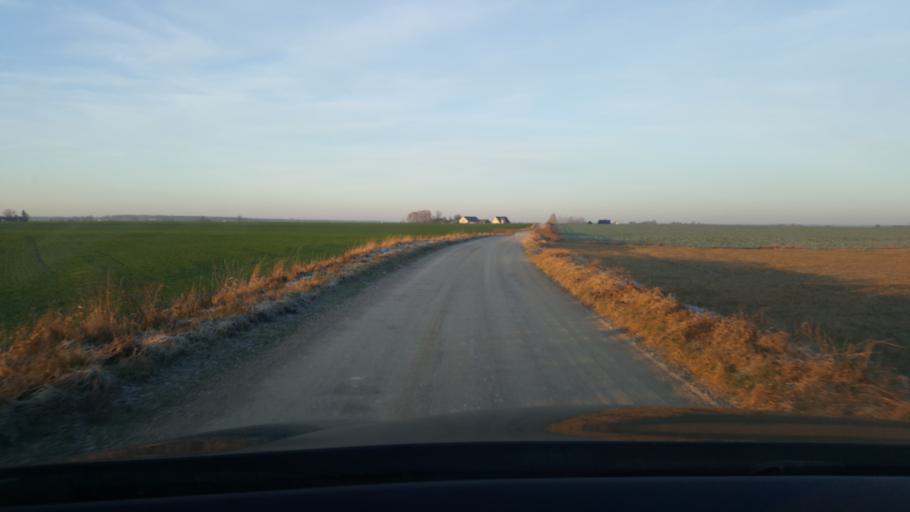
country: LT
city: Prienai
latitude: 54.4841
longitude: 23.9216
